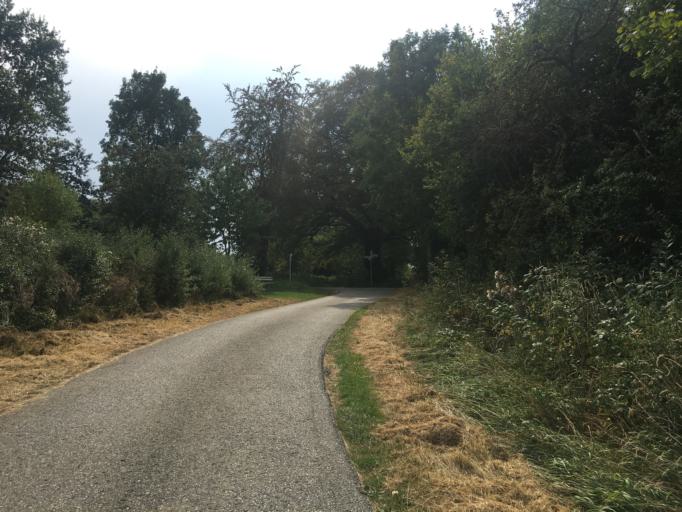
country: DE
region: Baden-Wuerttemberg
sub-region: Tuebingen Region
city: Hayingen
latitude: 48.2815
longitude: 9.4919
